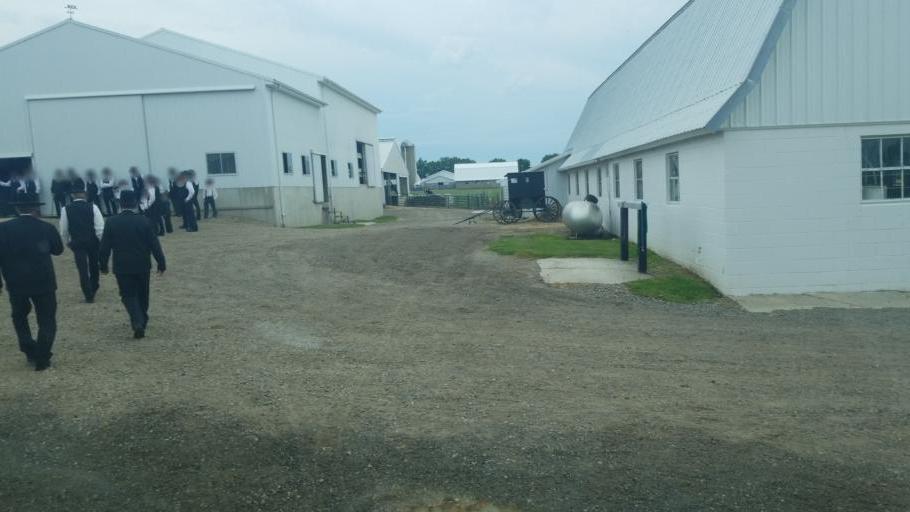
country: US
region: Michigan
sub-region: Barry County
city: Nashville
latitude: 42.6784
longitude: -84.9760
